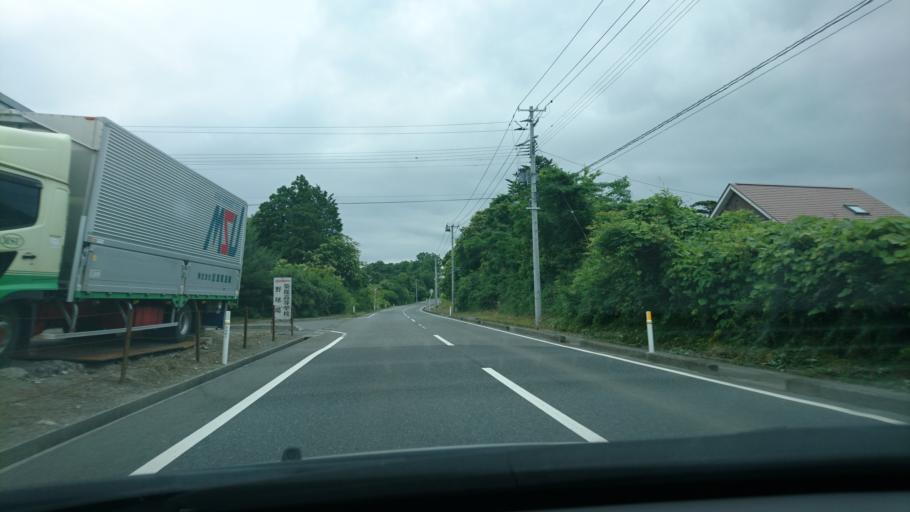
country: JP
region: Miyagi
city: Kogota
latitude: 38.7246
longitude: 141.0454
